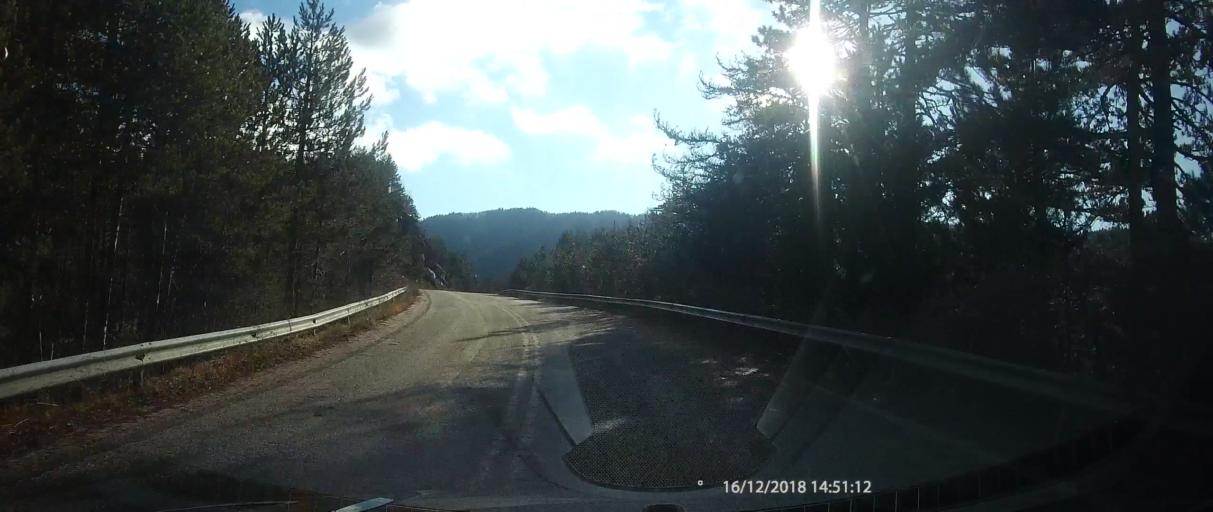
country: GR
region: West Macedonia
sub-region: Nomos Kastorias
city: Nestorio
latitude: 40.2063
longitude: 21.0738
